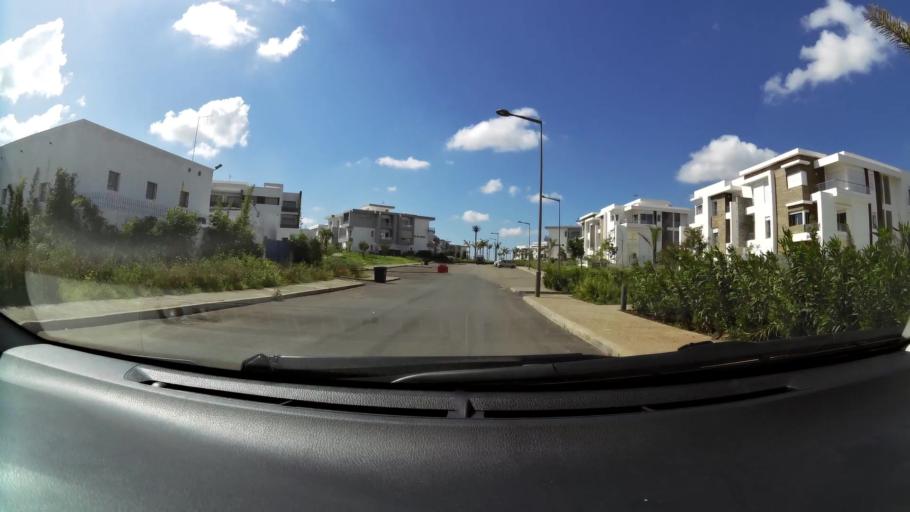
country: MA
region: Grand Casablanca
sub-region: Nouaceur
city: Bouskoura
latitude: 33.4741
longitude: -7.6038
